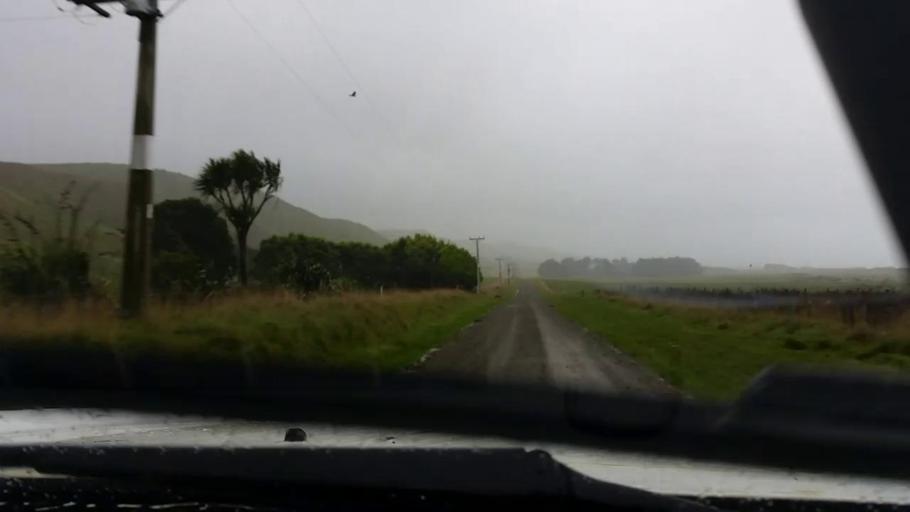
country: NZ
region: Wellington
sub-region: Masterton District
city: Masterton
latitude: -41.2574
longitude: 175.9037
